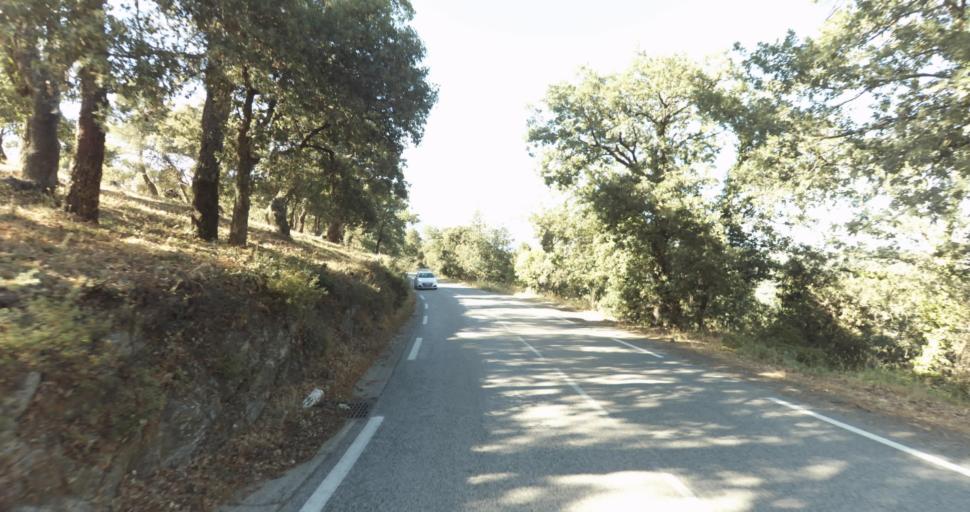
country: FR
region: Provence-Alpes-Cote d'Azur
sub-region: Departement du Var
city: Gassin
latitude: 43.2333
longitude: 6.5857
